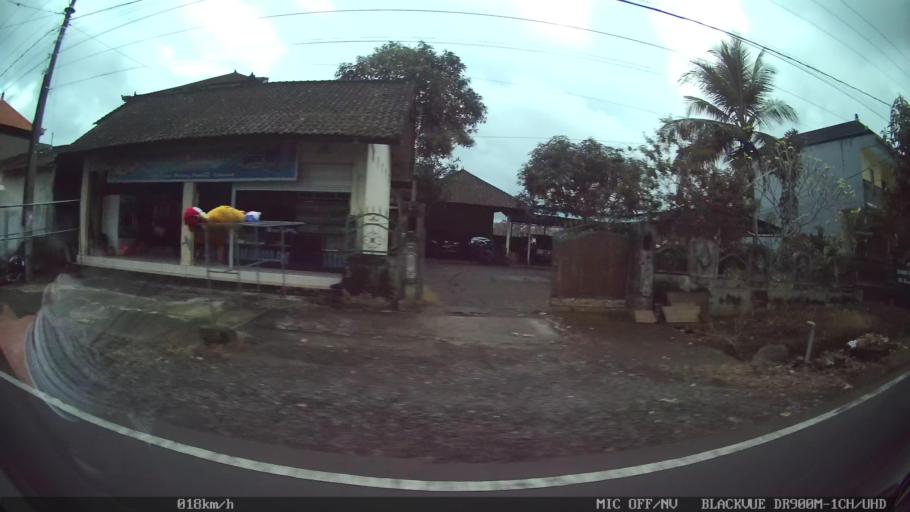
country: ID
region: Bali
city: Pohgending Kawan
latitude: -8.4422
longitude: 115.1411
